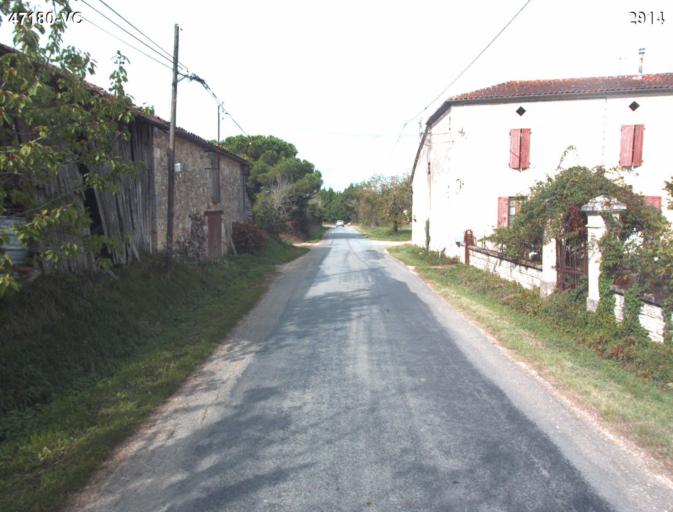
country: FR
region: Aquitaine
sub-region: Departement du Lot-et-Garonne
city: Sainte-Colombe-en-Bruilhois
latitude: 44.1698
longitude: 0.4510
